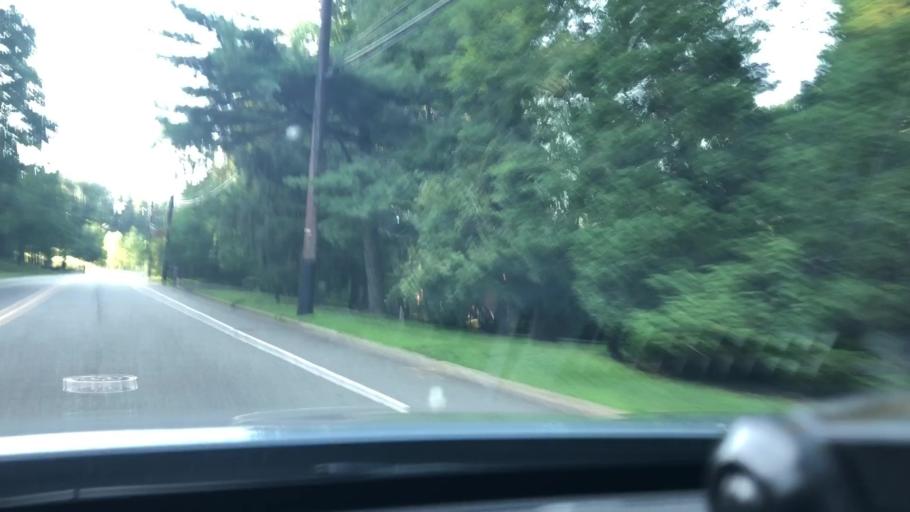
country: US
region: New Jersey
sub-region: Bergen County
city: Woodcliff Lake
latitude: 41.0168
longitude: -74.0698
